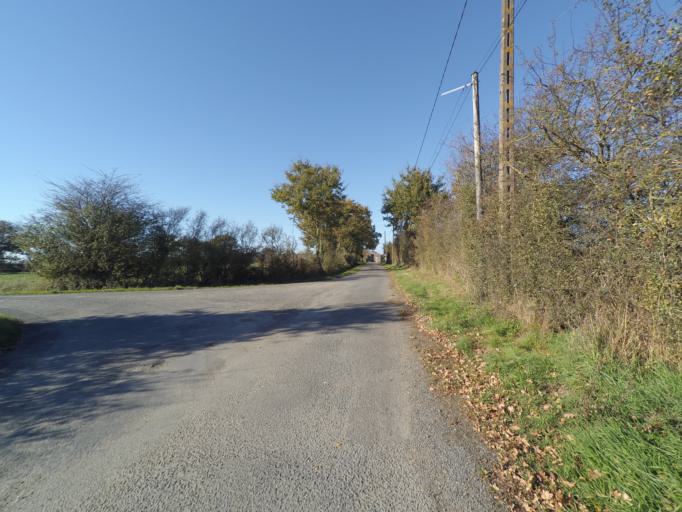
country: FR
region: Pays de la Loire
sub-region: Departement de la Vendee
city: Saint-Hilaire-de-Loulay
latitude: 46.9975
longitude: -1.3745
